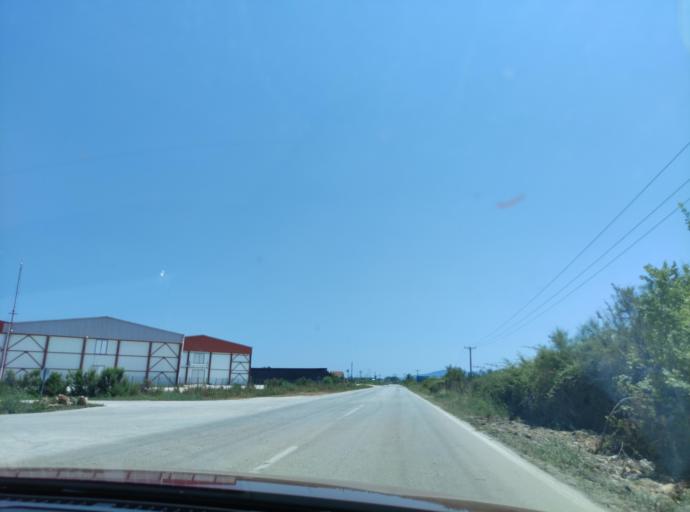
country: GR
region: East Macedonia and Thrace
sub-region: Nomos Kavalas
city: Keramoti
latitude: 40.8753
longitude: 24.6997
